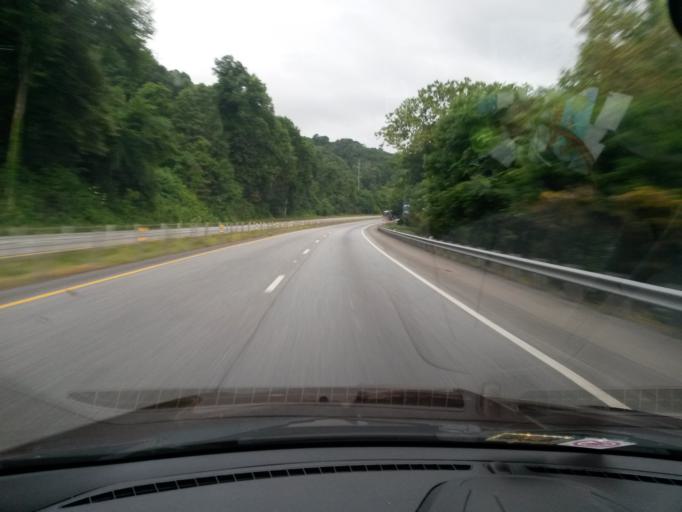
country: US
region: Virginia
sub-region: City of Covington
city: Fairlawn
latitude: 37.7784
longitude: -79.9143
